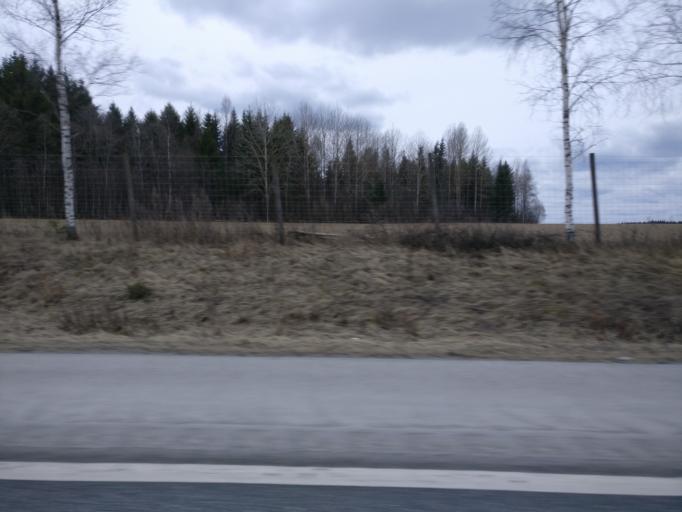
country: FI
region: Haeme
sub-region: Haemeenlinna
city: Janakkala
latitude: 60.8741
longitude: 24.5763
